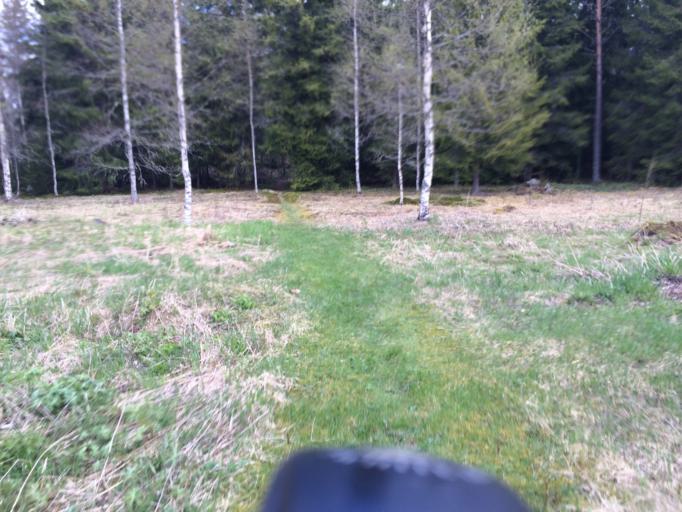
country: SE
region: OErebro
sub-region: Hallefors Kommun
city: Haellefors
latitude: 60.0404
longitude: 14.5250
